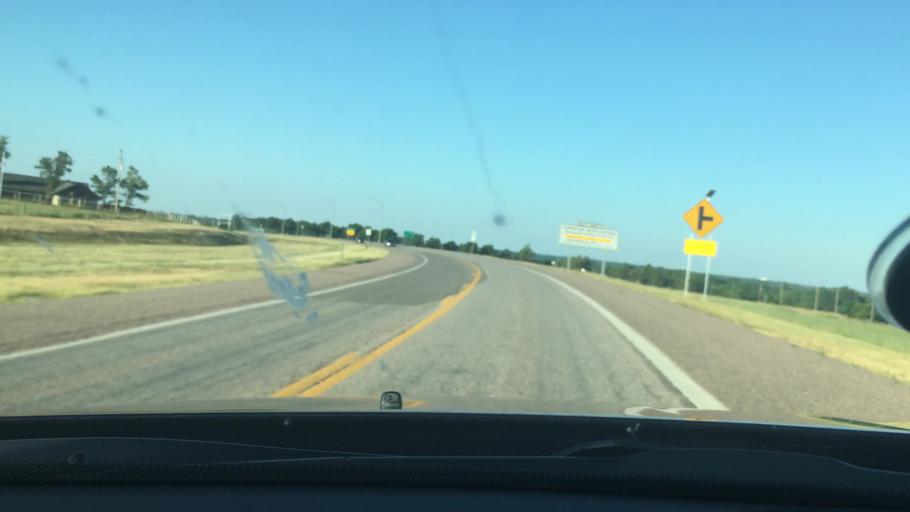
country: US
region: Oklahoma
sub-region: Pontotoc County
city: Ada
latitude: 34.6602
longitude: -96.7937
